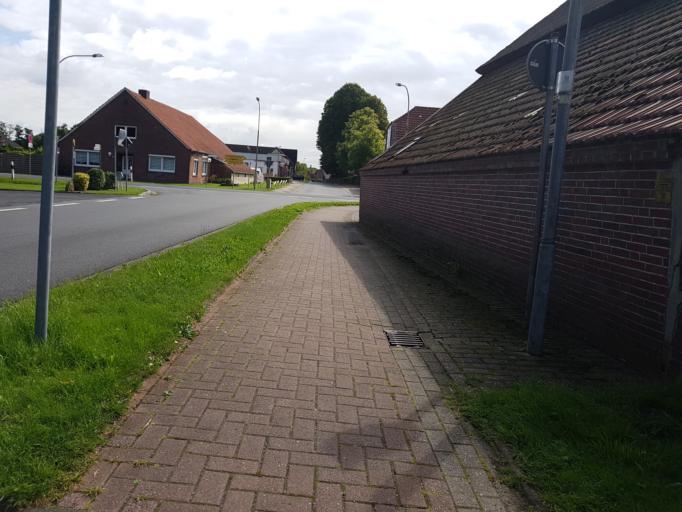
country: DE
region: Lower Saxony
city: Wittmund
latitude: 53.5296
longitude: 7.7810
